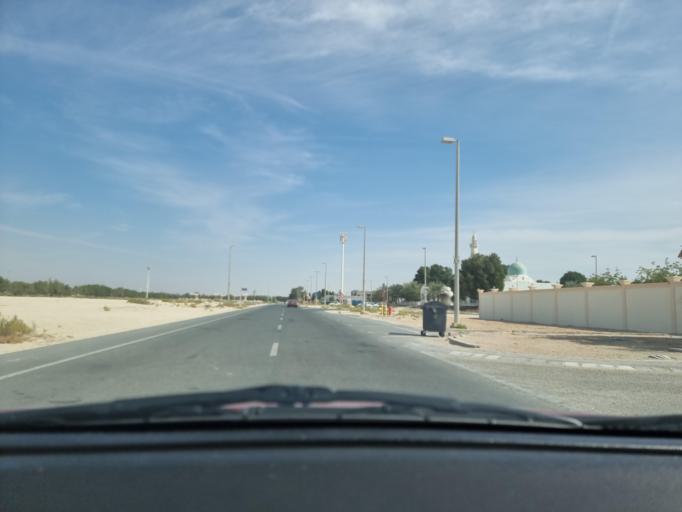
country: AE
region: Abu Dhabi
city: Abu Dhabi
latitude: 24.3844
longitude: 54.6988
